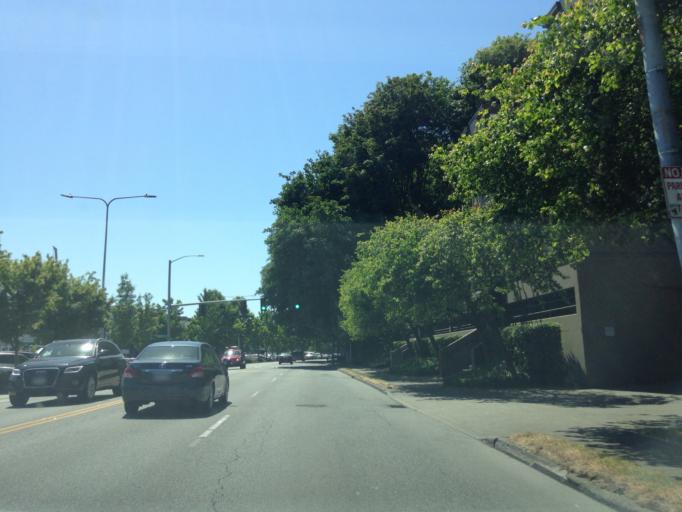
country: US
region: Washington
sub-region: King County
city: Seattle
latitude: 47.6385
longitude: -122.3412
